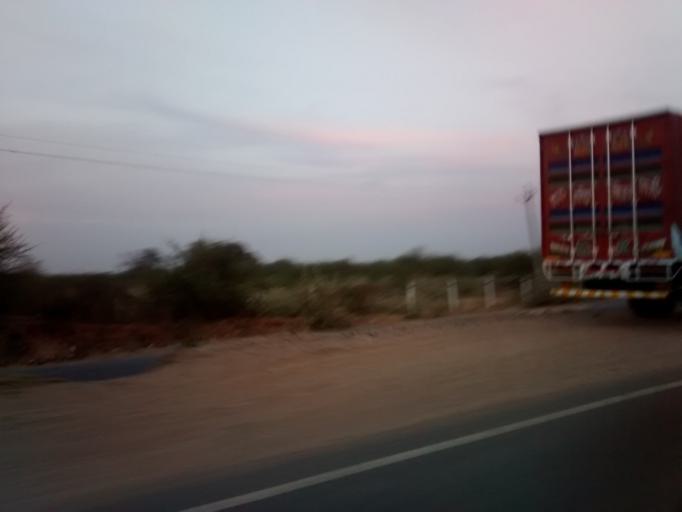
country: IN
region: Gujarat
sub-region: Ahmadabad
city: Naroda
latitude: 23.1137
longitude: 72.6662
